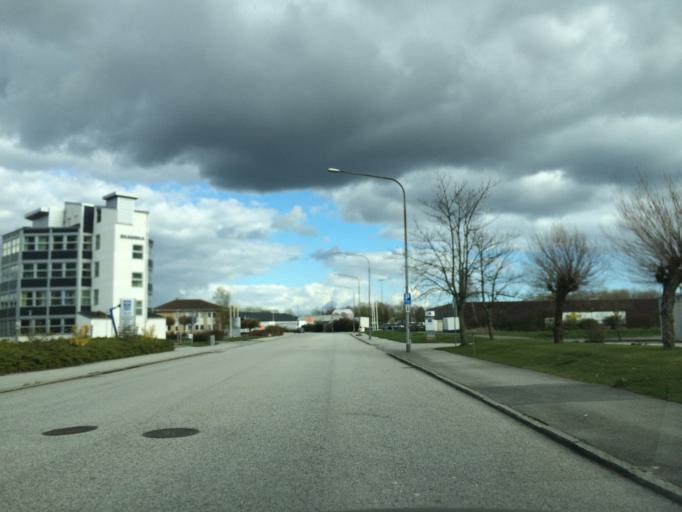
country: SE
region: Skane
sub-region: Lunds Kommun
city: Lund
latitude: 55.7173
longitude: 13.1598
